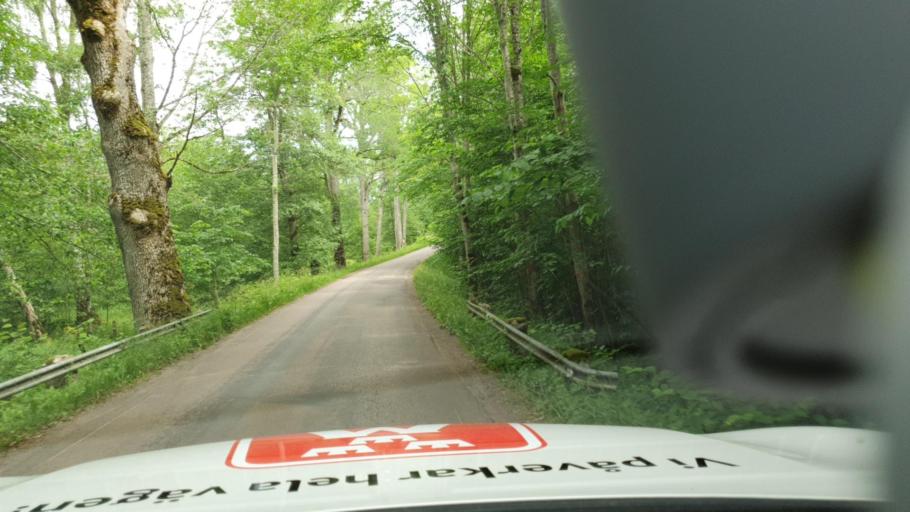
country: SE
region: Vaestra Goetaland
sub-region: Skara Kommun
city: Axvall
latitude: 58.4172
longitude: 13.6446
